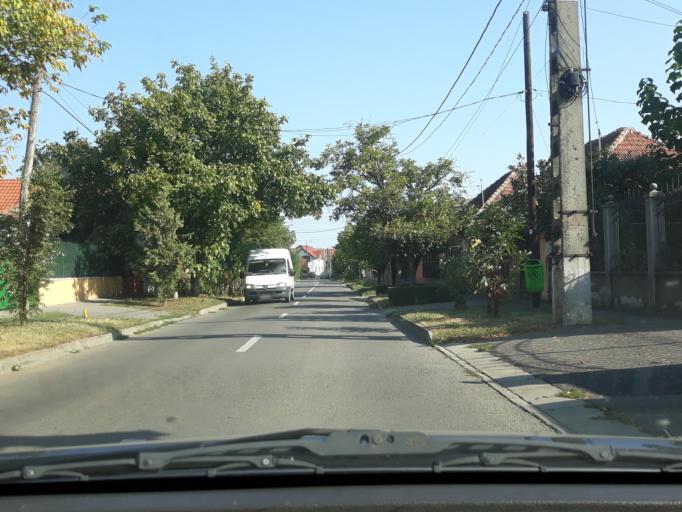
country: RO
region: Bihor
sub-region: Comuna Biharea
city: Oradea
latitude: 47.0344
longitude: 21.9394
